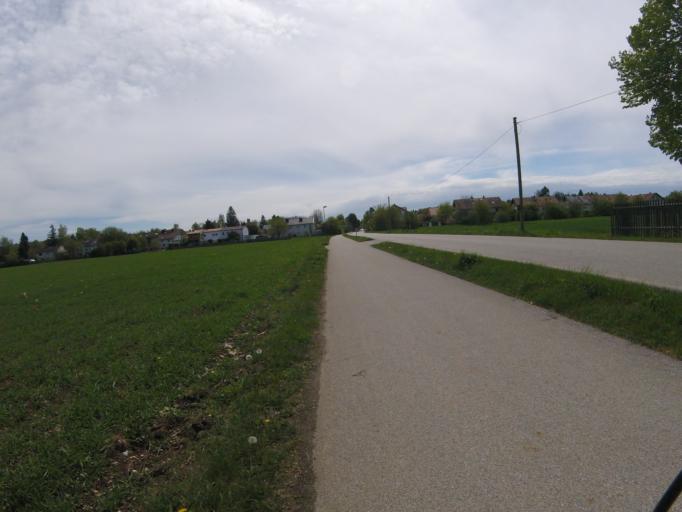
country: DE
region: Bavaria
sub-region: Upper Bavaria
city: Hohenbrunn
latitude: 48.0367
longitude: 11.7053
